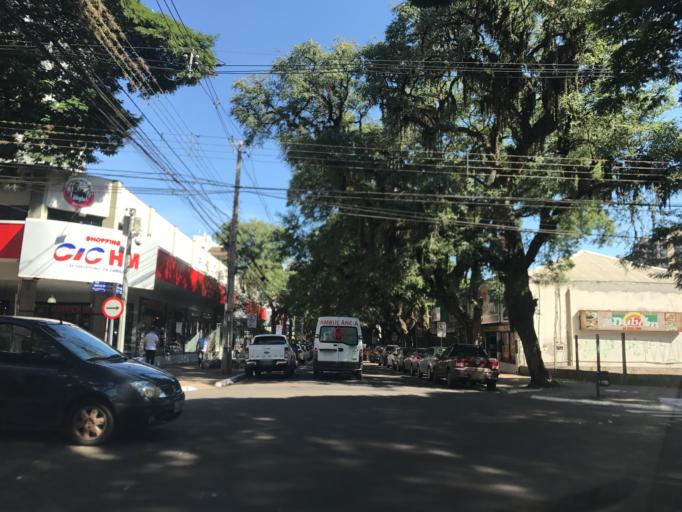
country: BR
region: Parana
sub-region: Maringa
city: Maringa
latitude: -23.4219
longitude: -51.9414
